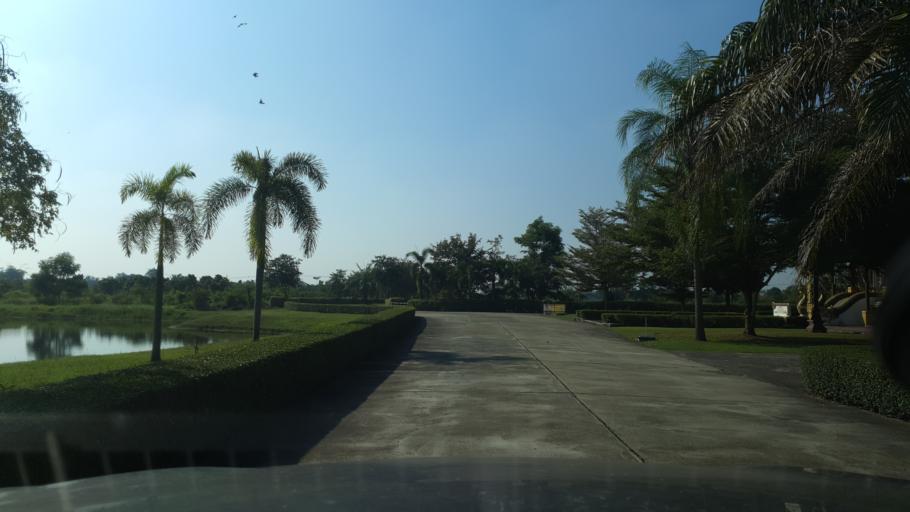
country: TH
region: Chiang Mai
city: Saraphi
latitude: 18.7112
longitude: 98.9751
